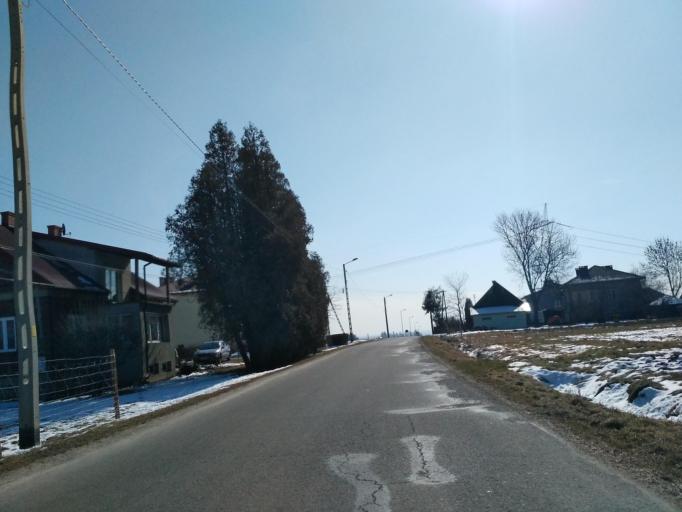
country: PL
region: Subcarpathian Voivodeship
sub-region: Powiat brzozowski
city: Jasienica Rosielna
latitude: 49.7688
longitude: 21.9216
